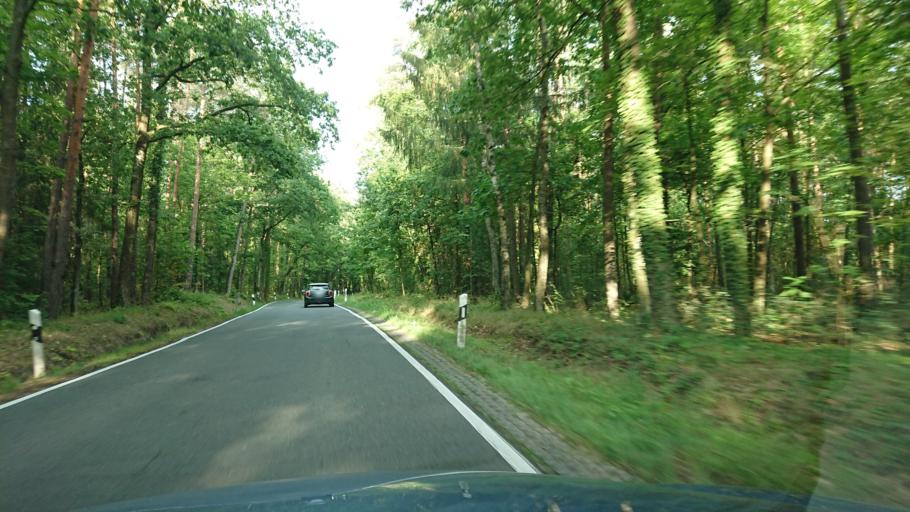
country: DE
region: Bavaria
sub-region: Regierungsbezirk Mittelfranken
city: Buckenhof
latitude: 49.6048
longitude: 11.0291
